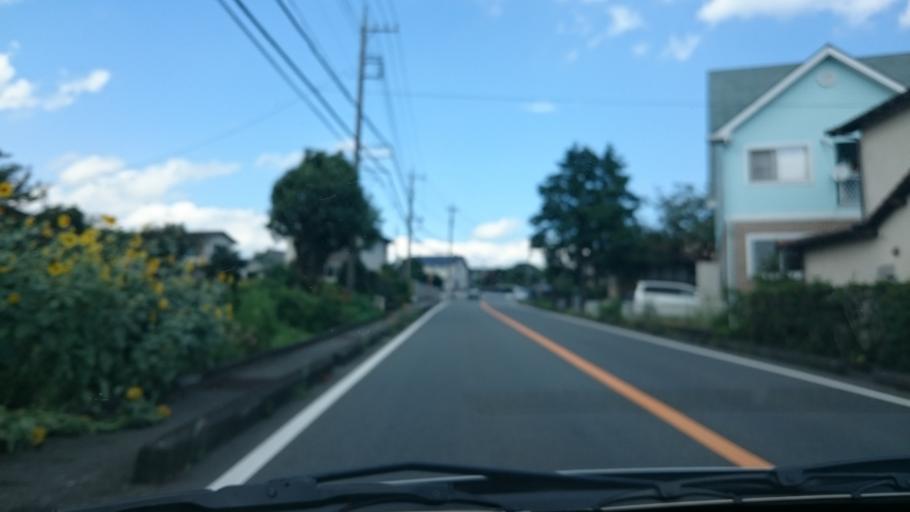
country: JP
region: Shizuoka
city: Gotemba
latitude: 35.2327
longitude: 138.9204
